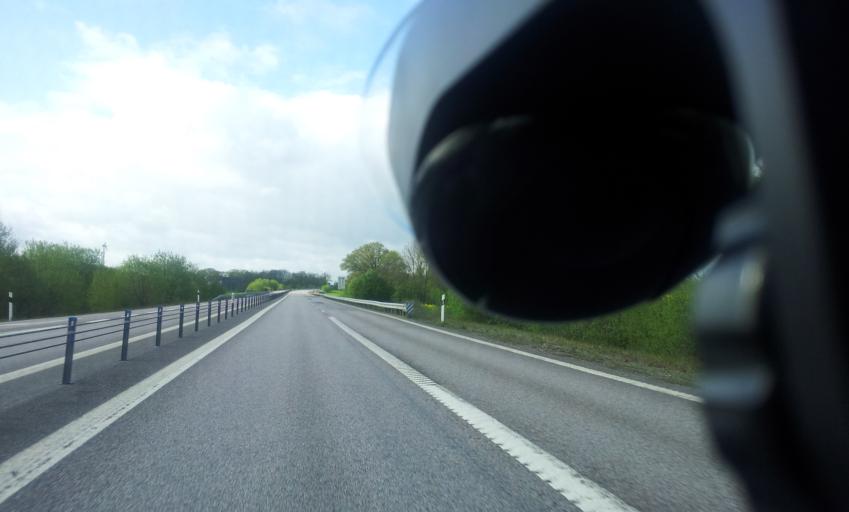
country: SE
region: Kalmar
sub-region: Torsas Kommun
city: Torsas
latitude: 56.4492
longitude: 16.0789
